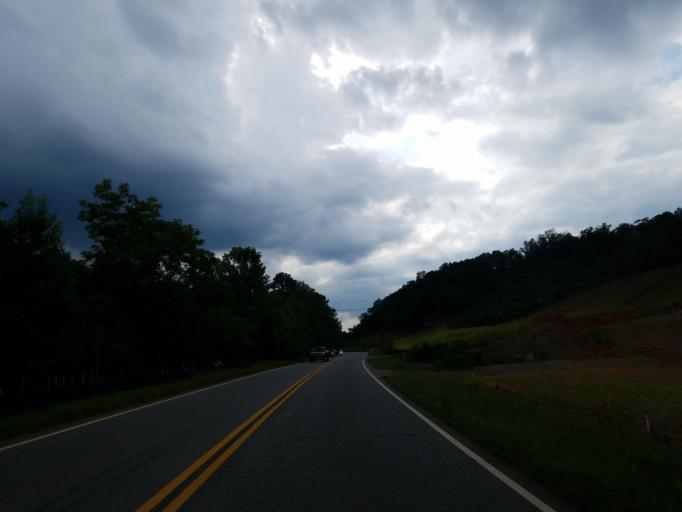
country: US
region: Georgia
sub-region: Floyd County
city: Shannon
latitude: 34.3688
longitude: -85.0154
